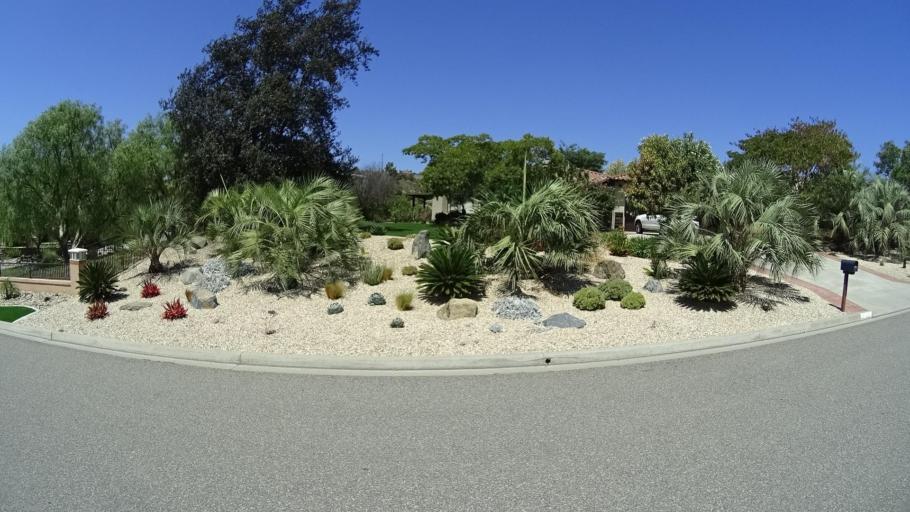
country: US
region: California
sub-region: San Diego County
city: Bonsall
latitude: 33.3262
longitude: -117.1957
